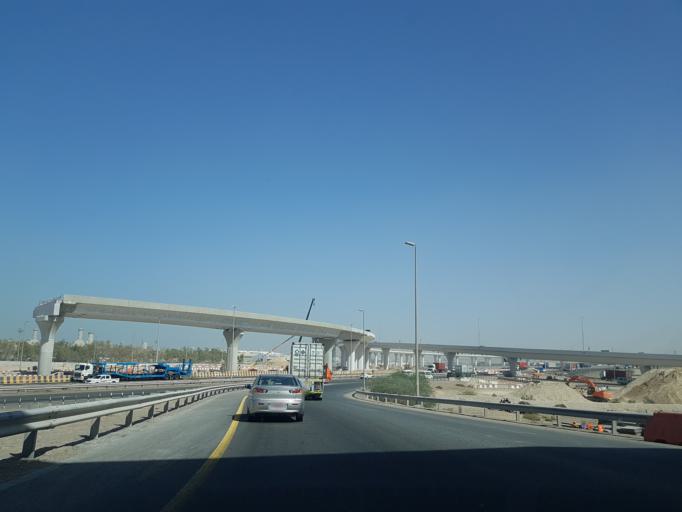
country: AE
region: Dubai
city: Dubai
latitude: 25.0132
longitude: 55.0932
